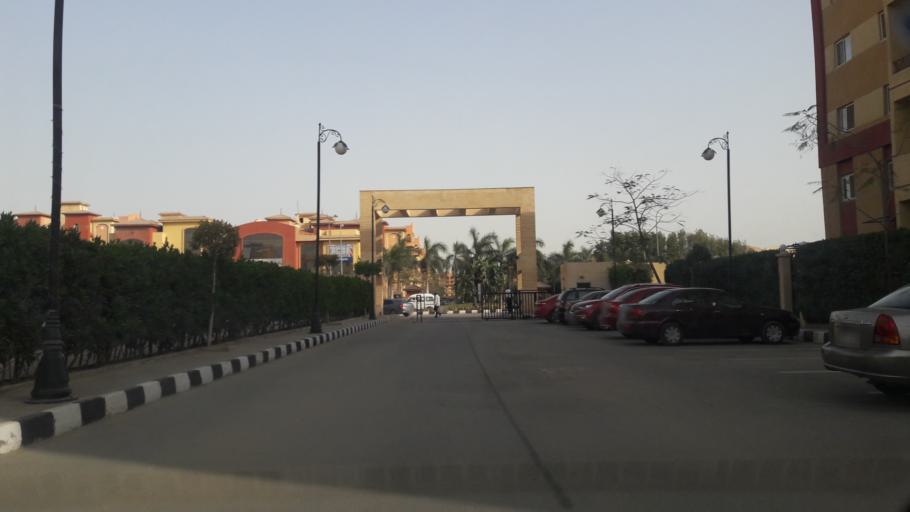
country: EG
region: Al Jizah
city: Madinat Sittah Uktubar
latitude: 29.9121
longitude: 31.0583
